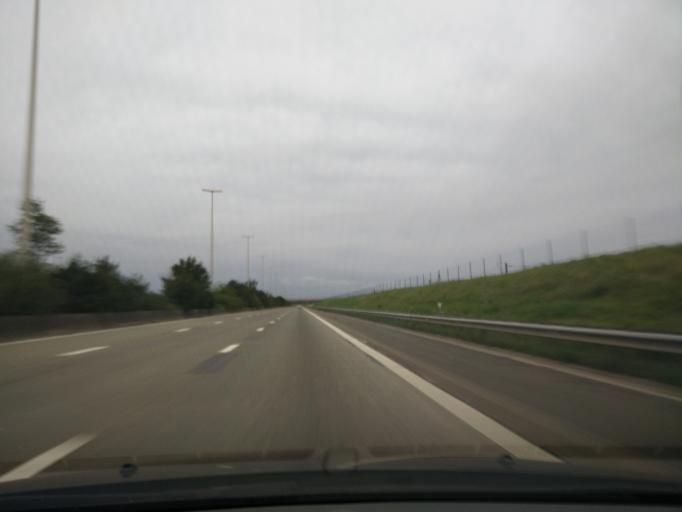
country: BE
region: Flanders
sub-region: Provincie Limburg
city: Gingelom
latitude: 50.7034
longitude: 5.1322
